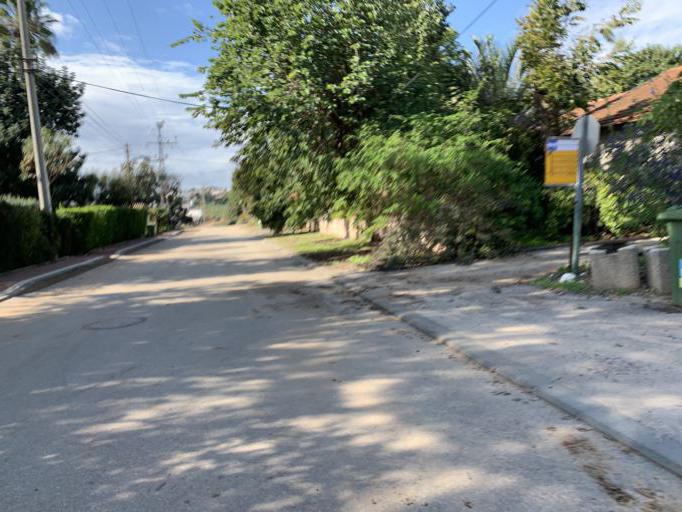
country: IL
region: Central District
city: Ra'anana
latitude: 32.1667
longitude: 34.8695
